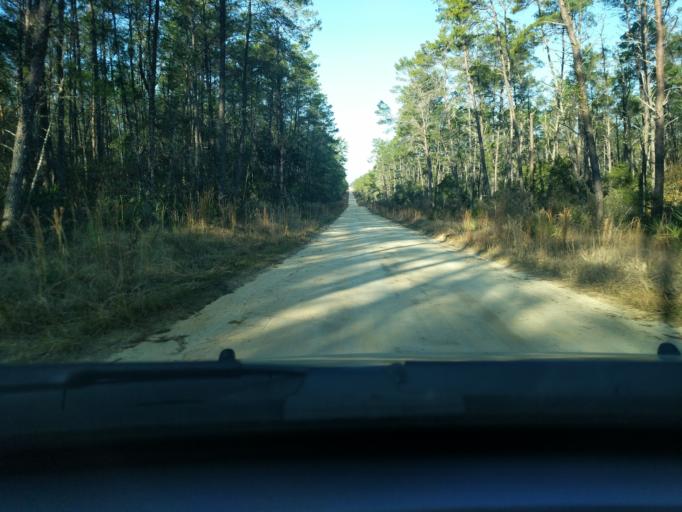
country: US
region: Florida
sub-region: Marion County
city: Silver Springs Shores
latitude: 29.2262
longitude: -81.7954
